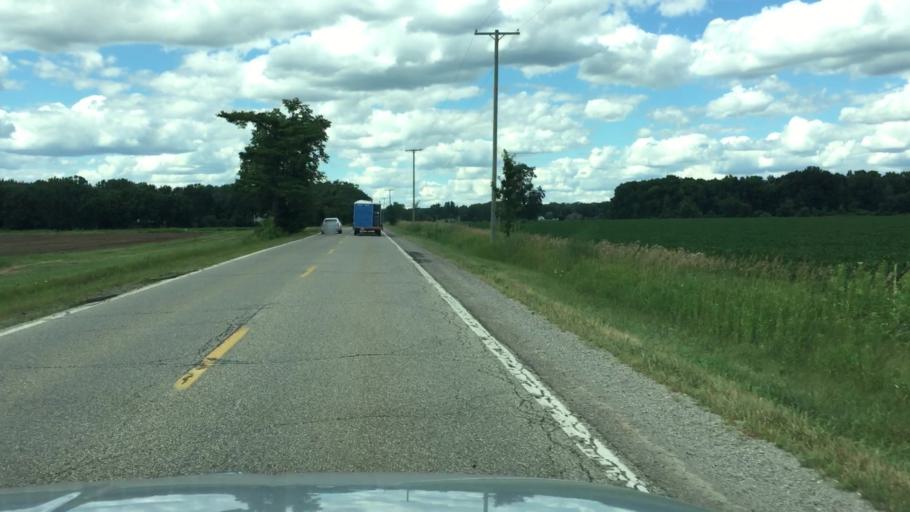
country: US
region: Michigan
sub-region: Macomb County
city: Armada
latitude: 42.8530
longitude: -82.9445
